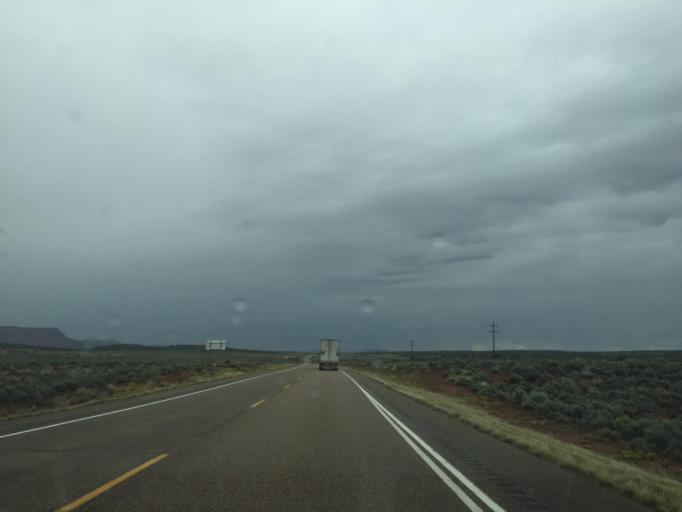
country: US
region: Utah
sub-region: Kane County
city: Kanab
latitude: 37.1234
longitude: -112.0994
